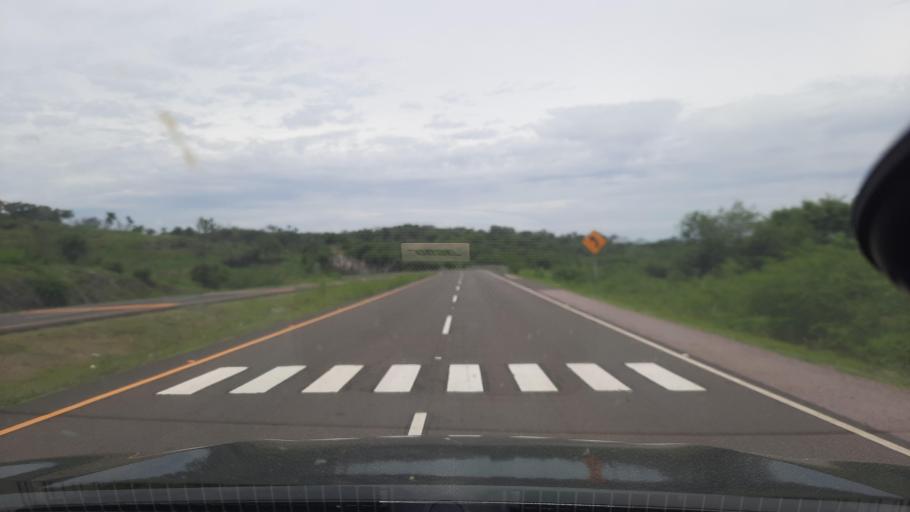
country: HN
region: Valle
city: Aramecina
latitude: 13.7396
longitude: -87.7198
